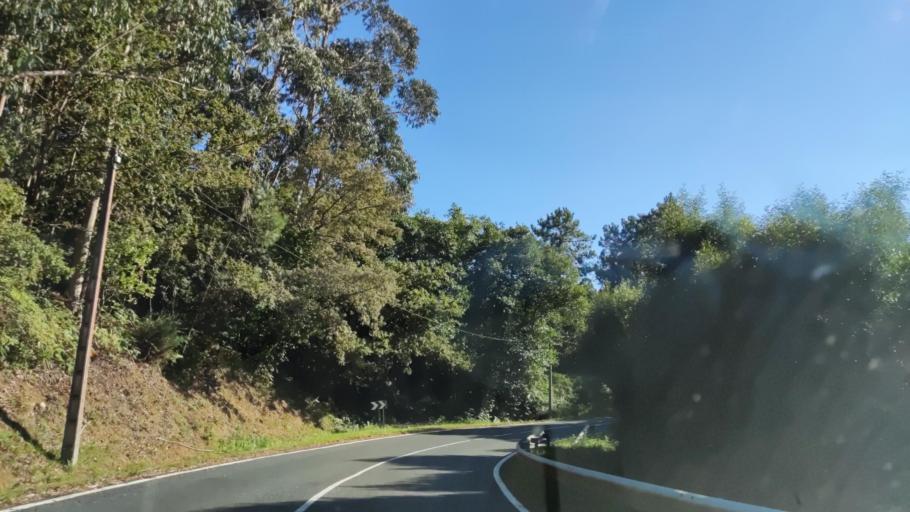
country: ES
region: Galicia
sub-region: Provincia da Coruna
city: Boiro
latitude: 42.5728
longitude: -9.0027
